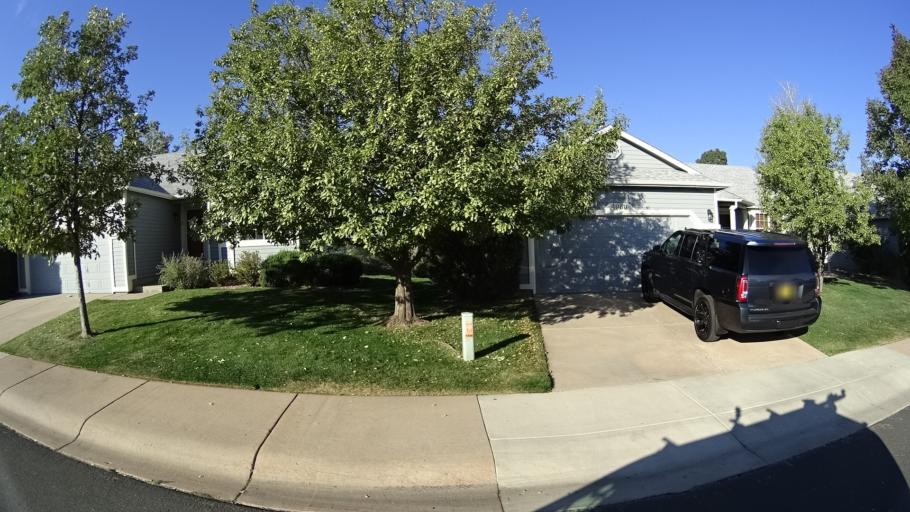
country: US
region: Colorado
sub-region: El Paso County
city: Cimarron Hills
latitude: 38.8904
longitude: -104.7080
